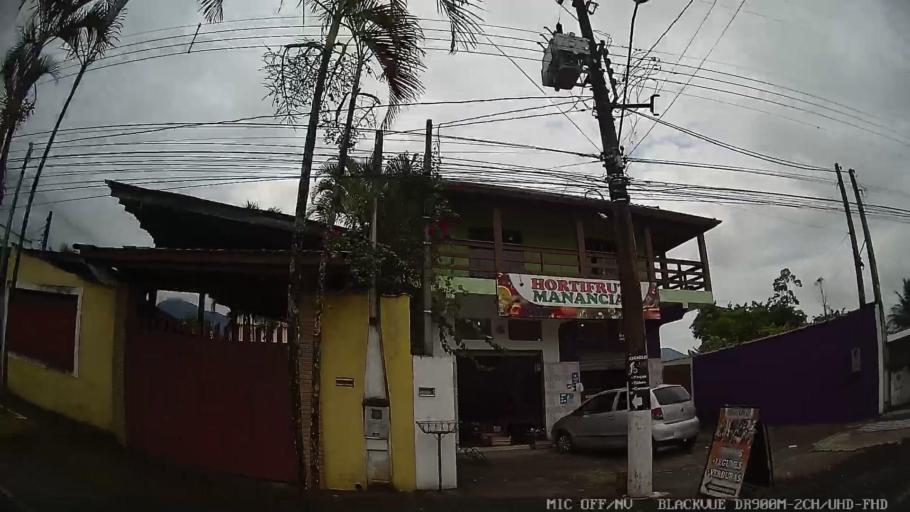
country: BR
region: Sao Paulo
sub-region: Sao Sebastiao
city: Sao Sebastiao
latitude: -23.7239
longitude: -45.4388
